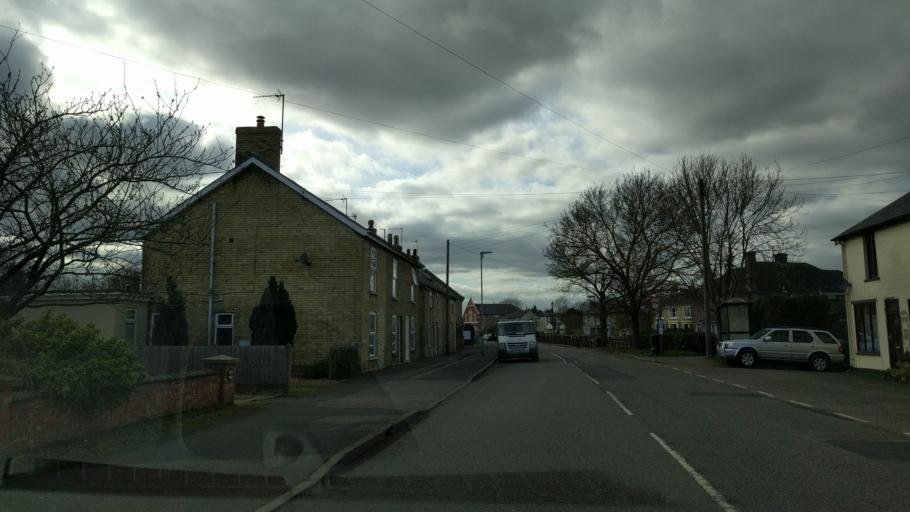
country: GB
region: England
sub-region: Cambridgeshire
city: Warboys
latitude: 52.4037
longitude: -0.0745
